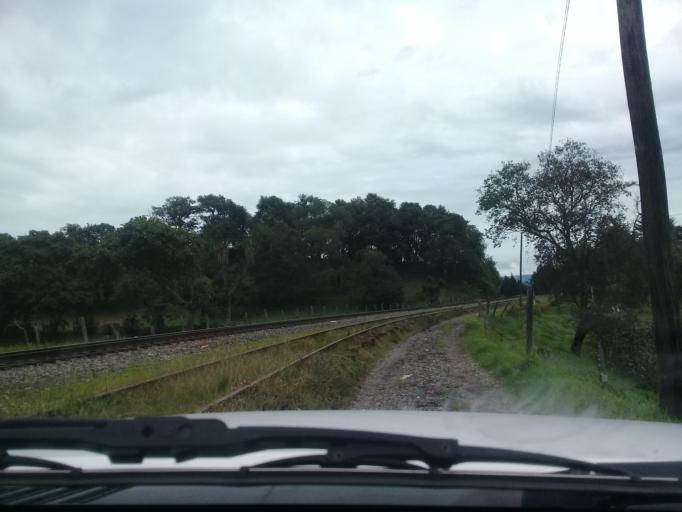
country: MX
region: Veracruz
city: Rafael Lucio
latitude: 19.6003
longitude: -96.9882
